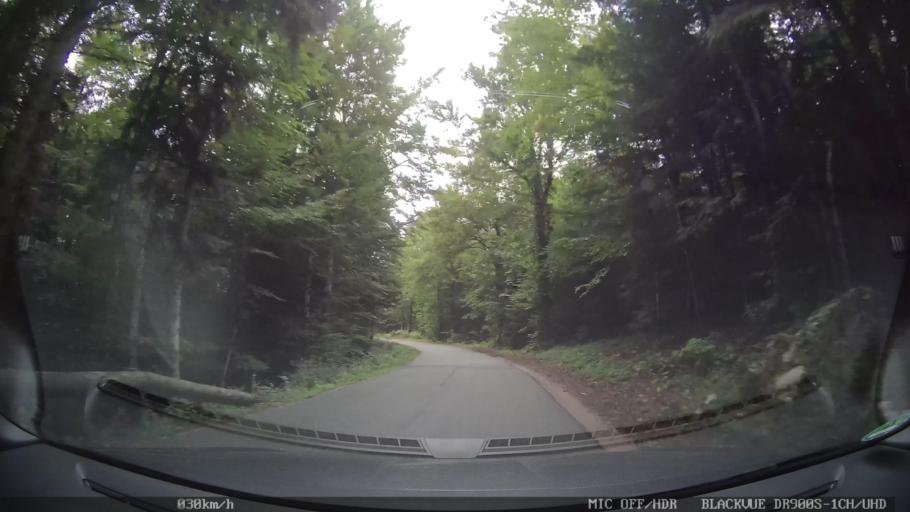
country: HR
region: Licko-Senjska
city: Jezerce
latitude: 44.9275
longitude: 15.5791
